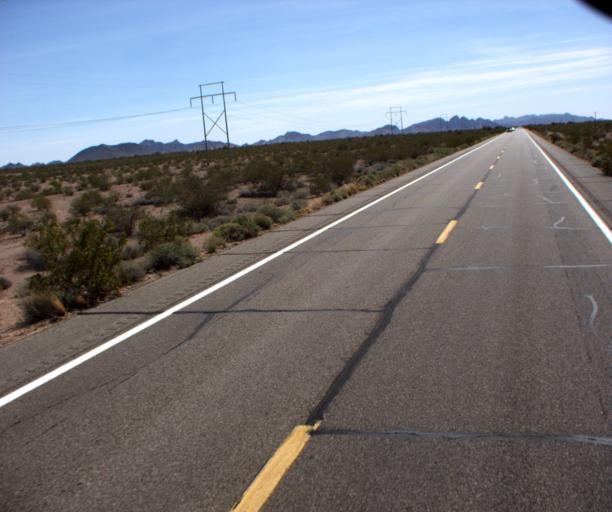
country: US
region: Arizona
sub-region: La Paz County
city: Quartzsite
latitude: 33.3995
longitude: -114.2172
